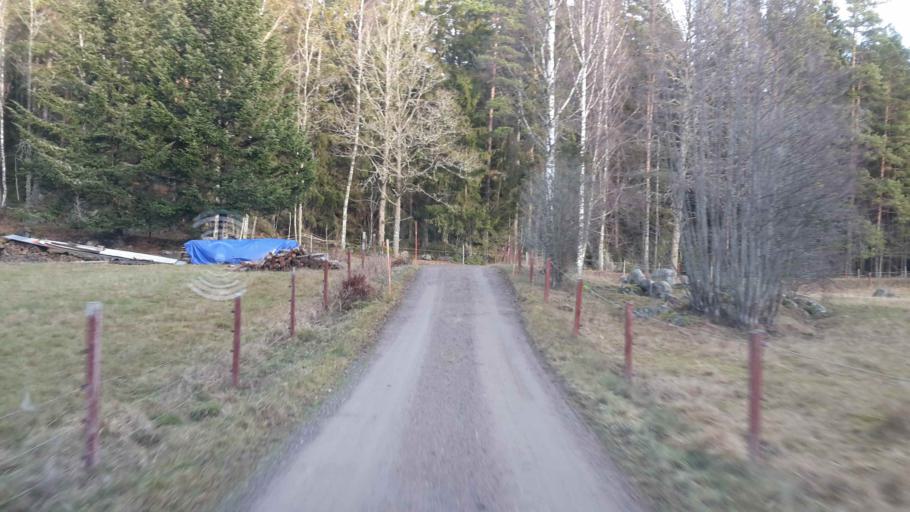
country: SE
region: OEstergoetland
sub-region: Atvidabergs Kommun
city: Atvidaberg
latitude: 58.2860
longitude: 16.0893
